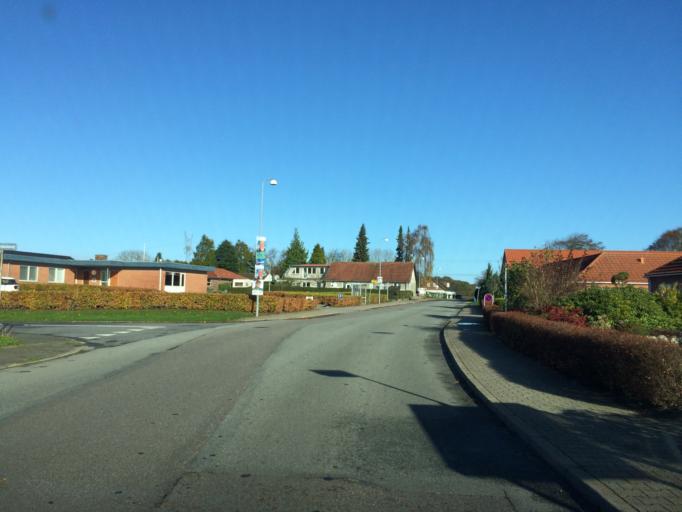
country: DK
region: South Denmark
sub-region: Fredericia Kommune
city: Taulov
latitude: 55.5465
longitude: 9.6168
